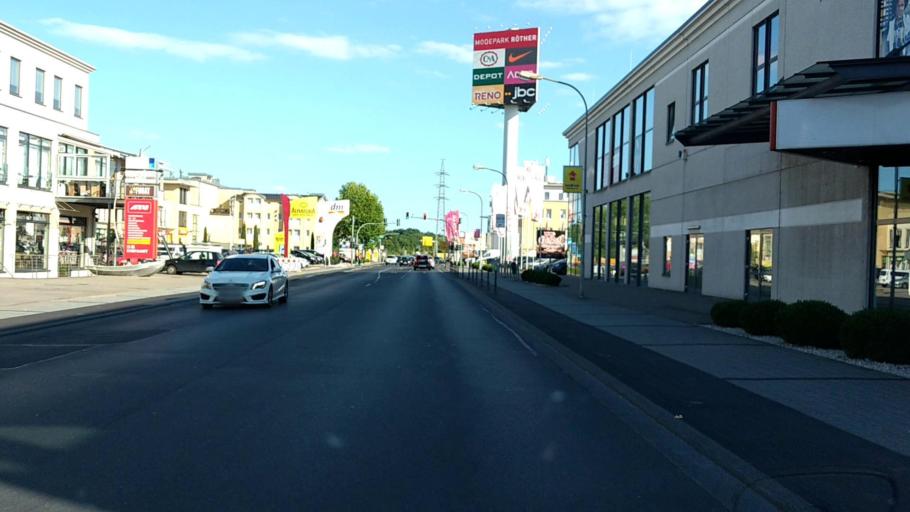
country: DE
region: North Rhine-Westphalia
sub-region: Regierungsbezirk Koln
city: Kerpen
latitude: 50.9009
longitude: 6.6795
